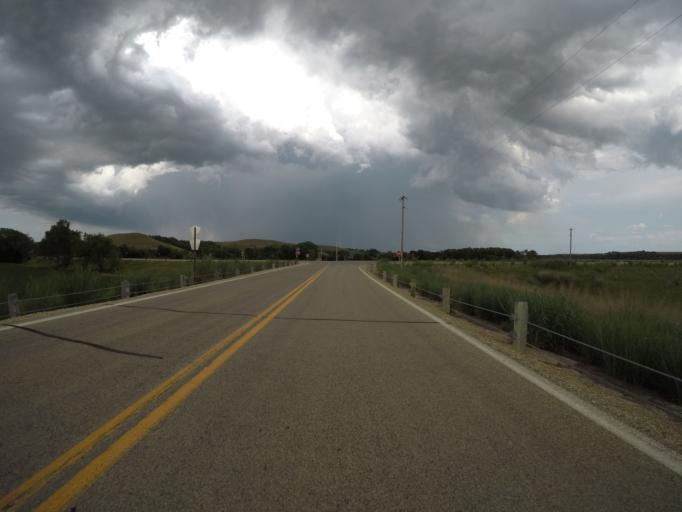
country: US
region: Kansas
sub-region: Marshall County
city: Blue Rapids
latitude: 39.4793
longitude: -96.8307
